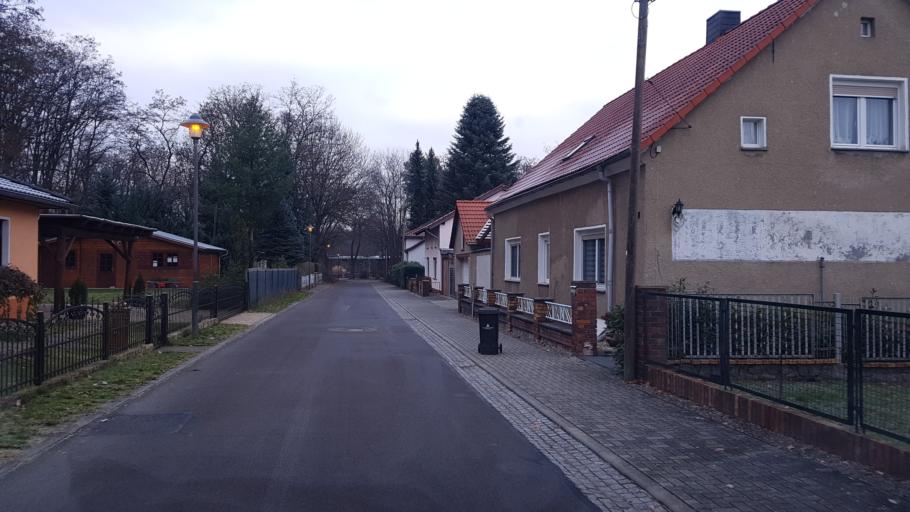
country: DE
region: Brandenburg
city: Schipkau
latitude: 51.5425
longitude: 13.8880
